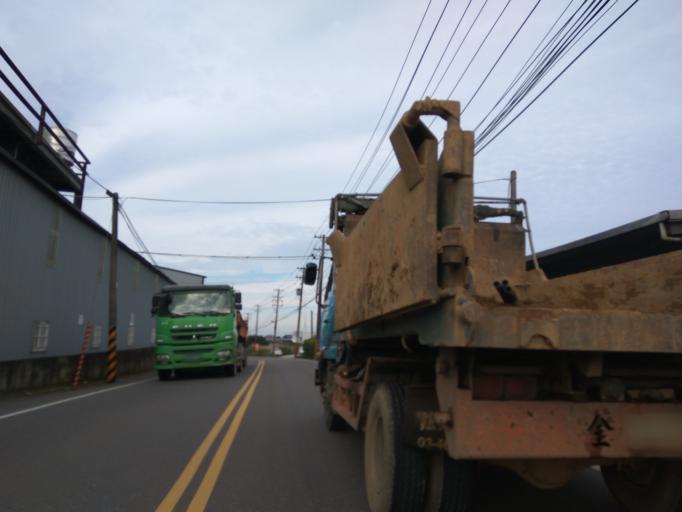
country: TW
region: Taiwan
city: Daxi
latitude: 24.9446
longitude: 121.1494
